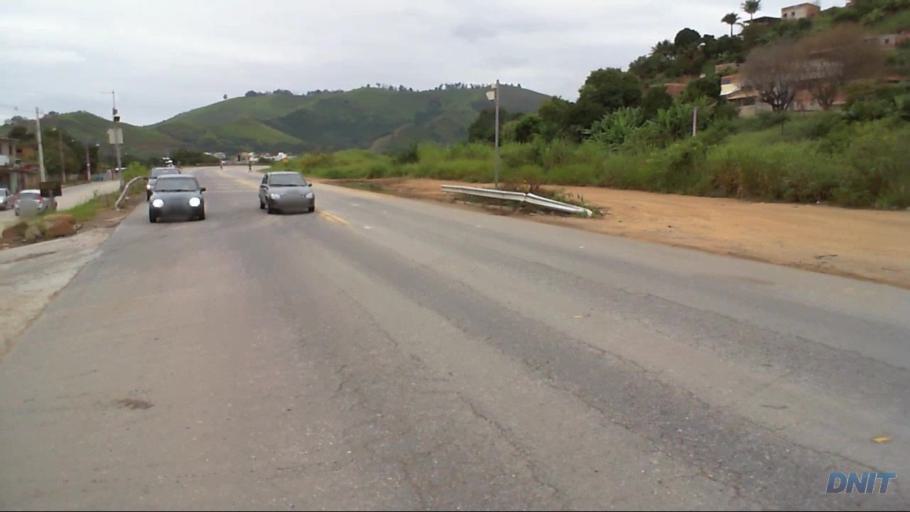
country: BR
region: Minas Gerais
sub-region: Coronel Fabriciano
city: Coronel Fabriciano
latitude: -19.5302
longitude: -42.6193
